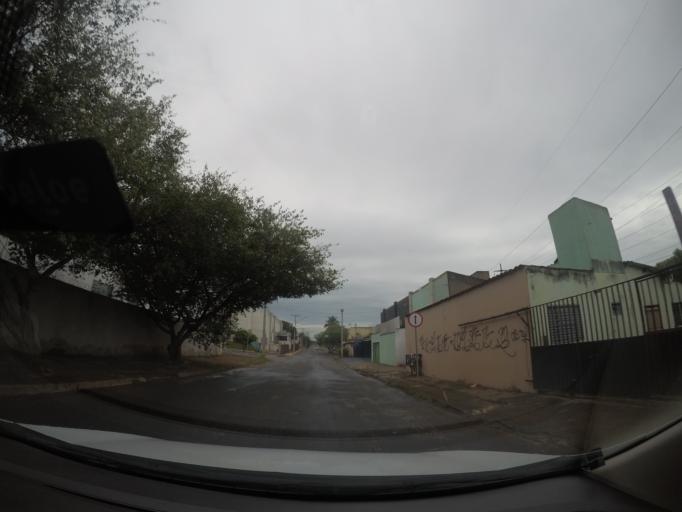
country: BR
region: Goias
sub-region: Goiania
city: Goiania
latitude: -16.6500
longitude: -49.2627
